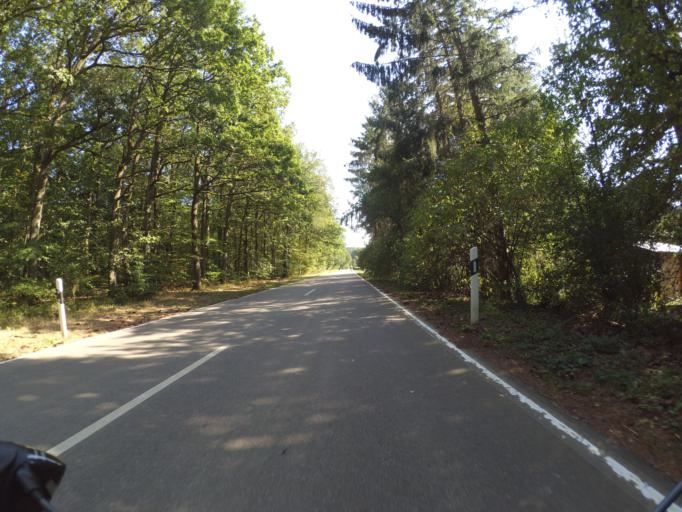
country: DE
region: Rheinland-Pfalz
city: Burgen
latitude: 49.8591
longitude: 6.9755
